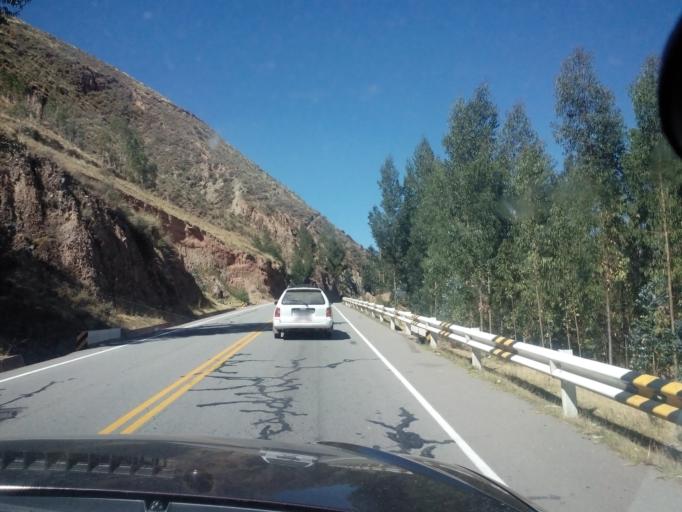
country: PE
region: Cusco
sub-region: Provincia de Canchis
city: Checacupe
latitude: -14.0343
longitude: -71.4505
